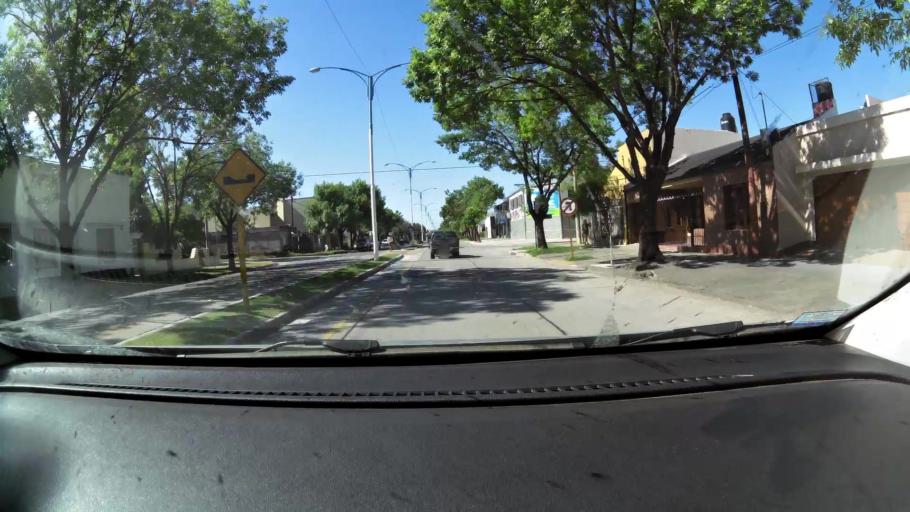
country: AR
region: Santa Fe
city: Rafaela
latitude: -31.2428
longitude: -61.4894
